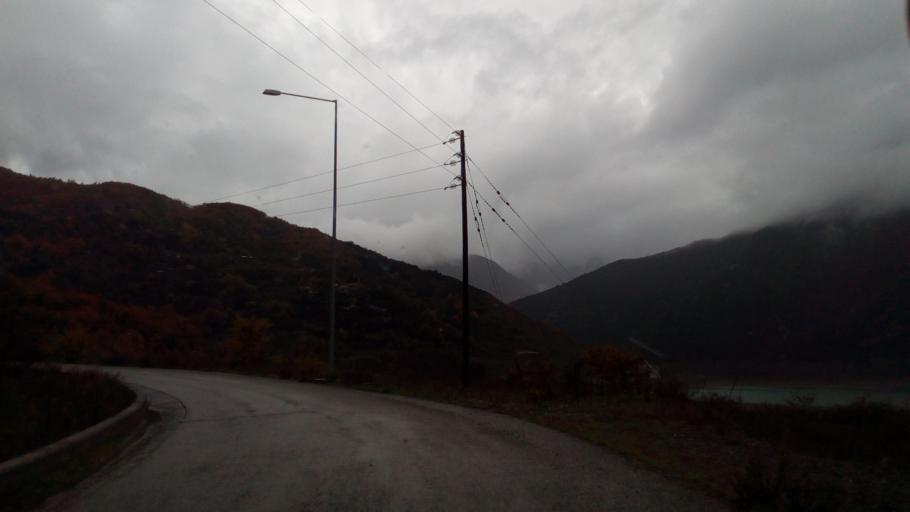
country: GR
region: West Greece
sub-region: Nomos Aitolias kai Akarnanias
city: Thermo
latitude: 38.6617
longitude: 21.8471
